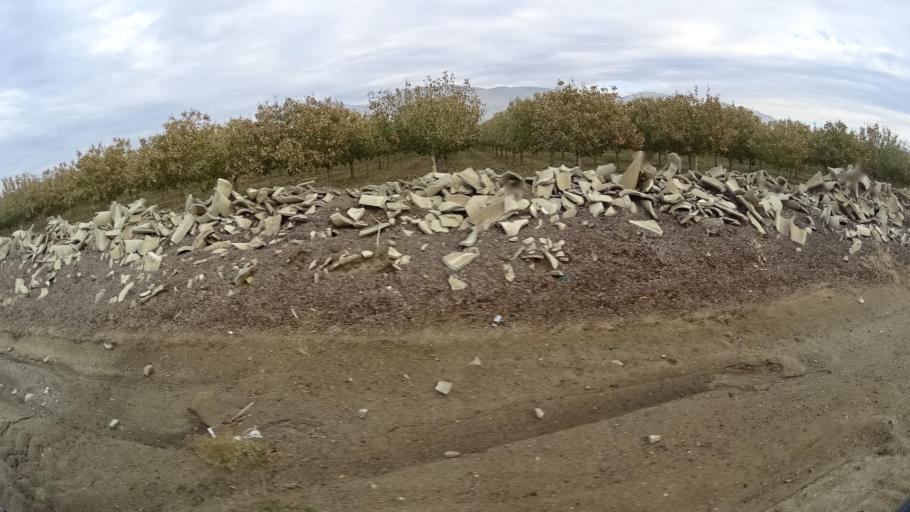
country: US
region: California
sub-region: Kern County
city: Arvin
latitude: 35.1595
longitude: -118.8236
